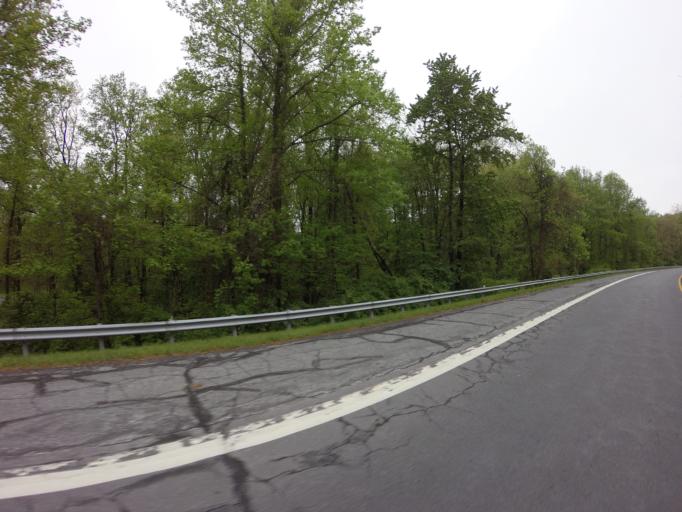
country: US
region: Maryland
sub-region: Frederick County
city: Braddock Heights
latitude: 39.4265
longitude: -77.4854
